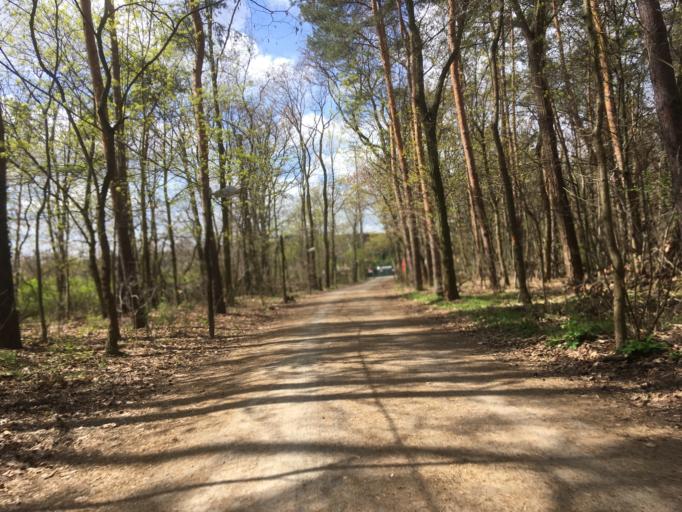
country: DE
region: Berlin
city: Kopenick Bezirk
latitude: 52.4592
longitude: 13.5705
